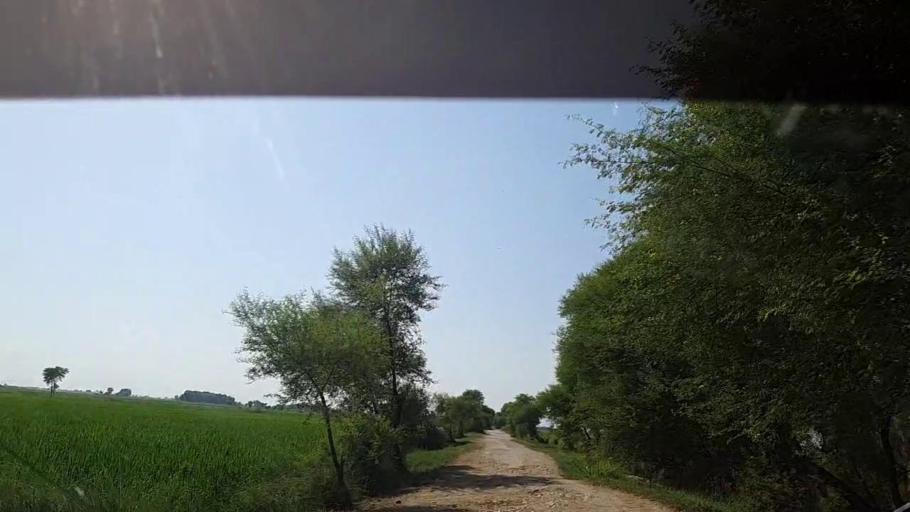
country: PK
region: Sindh
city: Ghauspur
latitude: 28.1779
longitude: 69.0392
